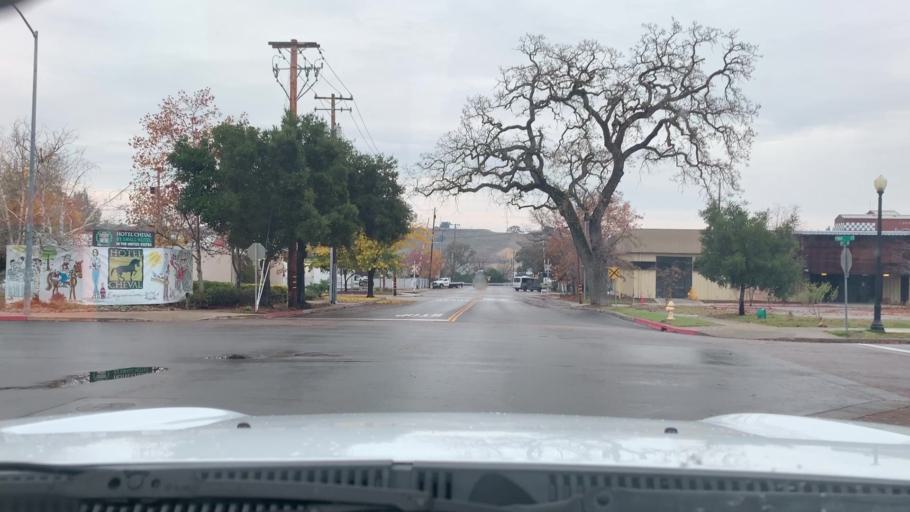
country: US
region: California
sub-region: San Luis Obispo County
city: Paso Robles
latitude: 35.6247
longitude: -120.6888
